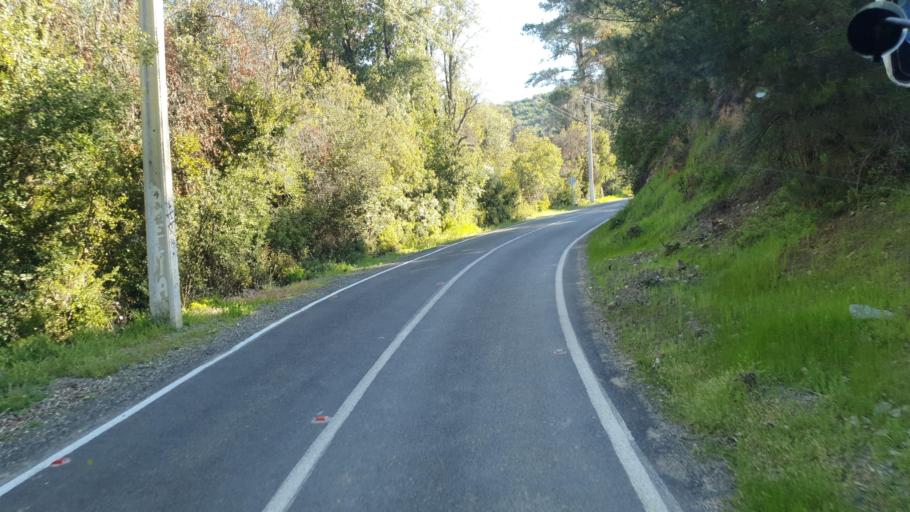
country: CL
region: Valparaiso
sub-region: Provincia de Marga Marga
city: Limache
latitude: -33.1782
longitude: -71.1711
